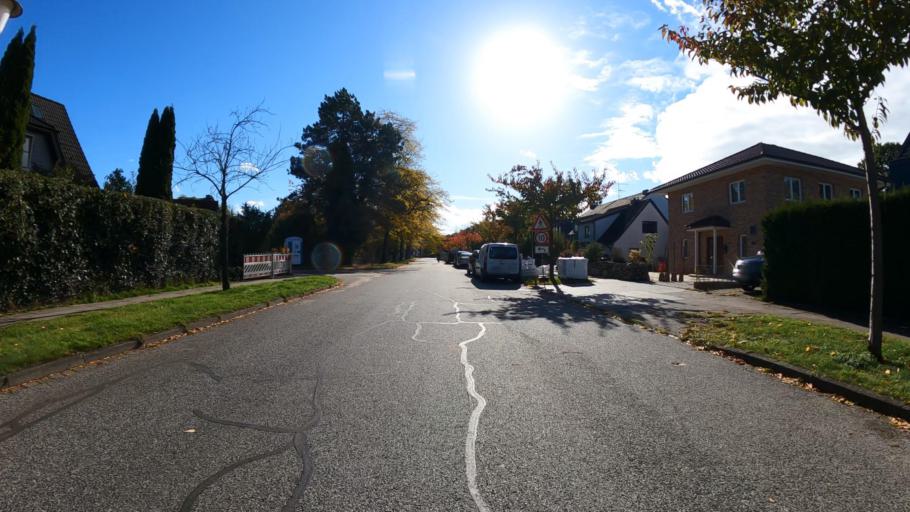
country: DE
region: Schleswig-Holstein
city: Ahrensburg
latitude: 53.6808
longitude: 10.2230
